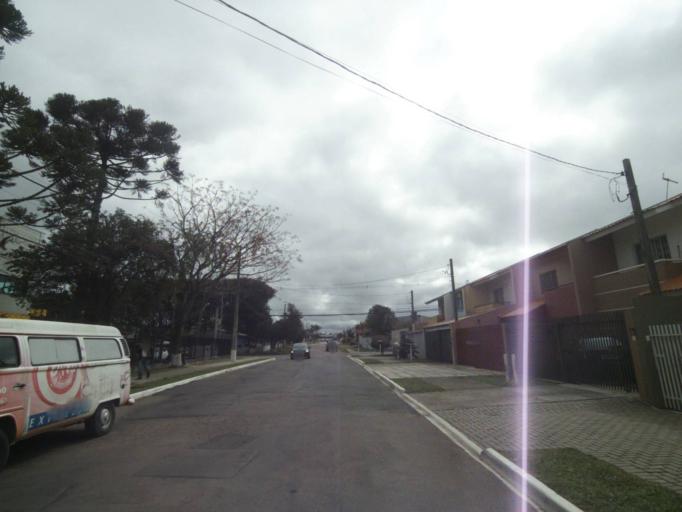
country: BR
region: Parana
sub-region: Sao Jose Dos Pinhais
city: Sao Jose dos Pinhais
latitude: -25.5386
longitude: -49.2966
